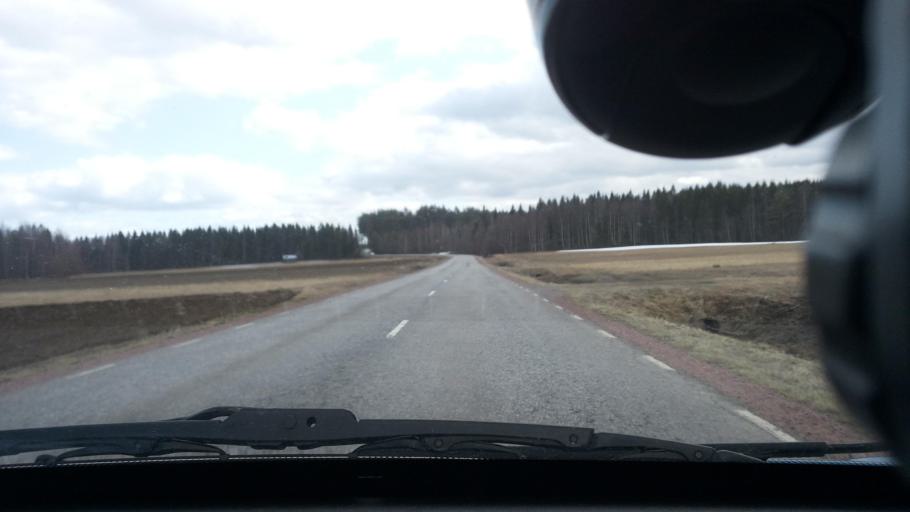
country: SE
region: Norrbotten
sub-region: Bodens Kommun
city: Saevast
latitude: 65.6715
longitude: 21.8072
